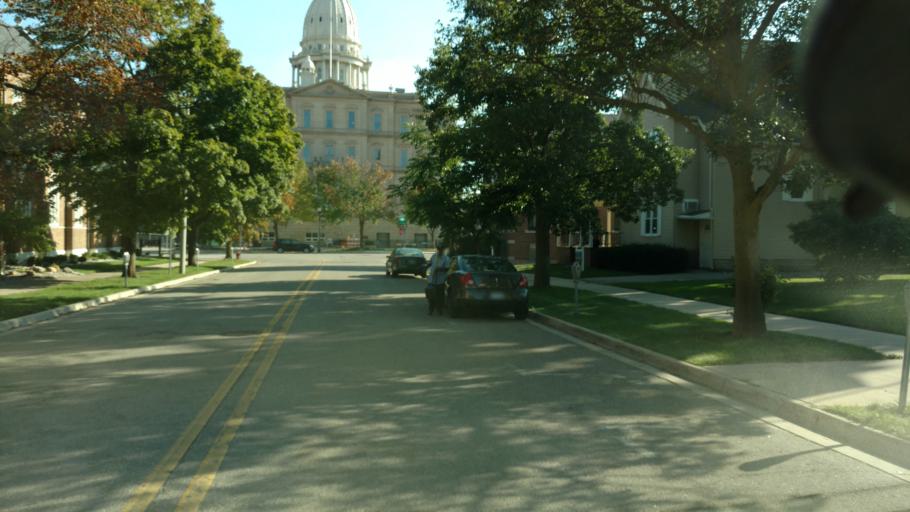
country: US
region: Michigan
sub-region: Ingham County
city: Lansing
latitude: 42.7353
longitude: -84.5554
